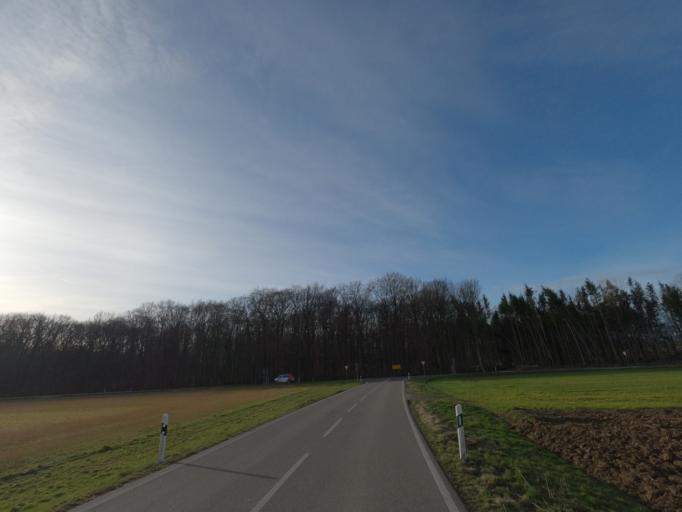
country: DE
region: Baden-Wuerttemberg
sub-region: Regierungsbezirk Stuttgart
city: Hattenhofen
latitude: 48.6700
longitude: 9.5924
